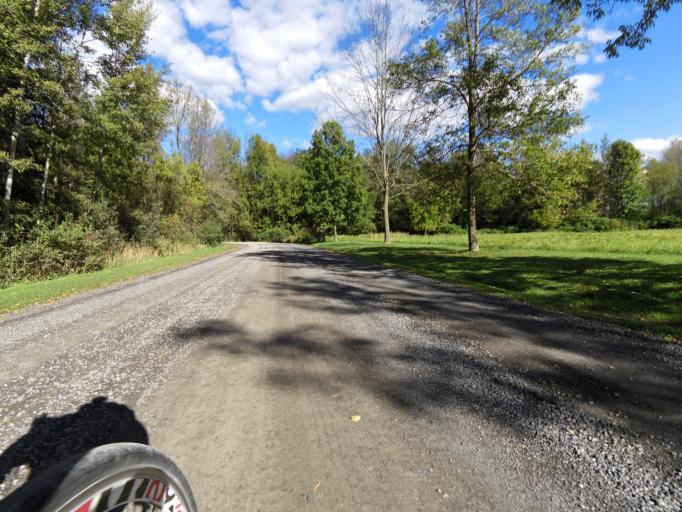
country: CA
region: Ontario
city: Bells Corners
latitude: 45.1006
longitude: -75.6235
